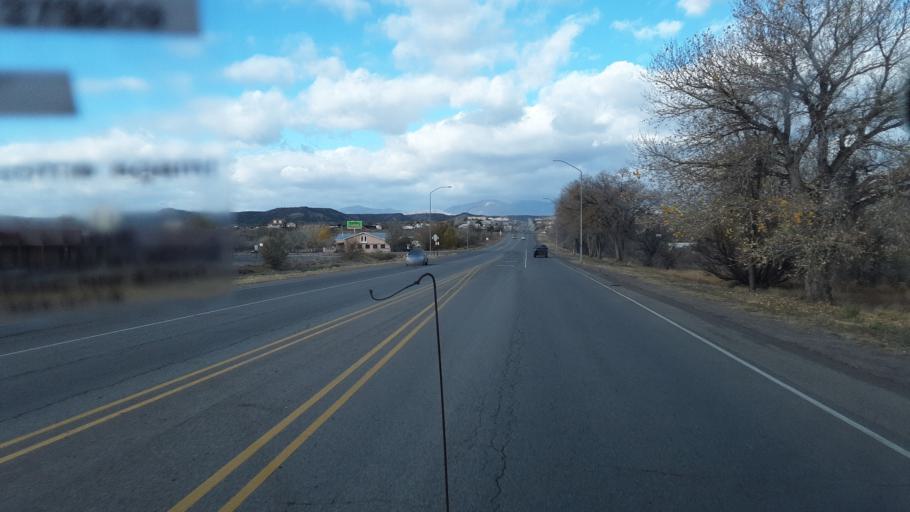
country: US
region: New Mexico
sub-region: Rio Arriba County
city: Espanola
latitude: 36.0083
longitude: -106.0783
